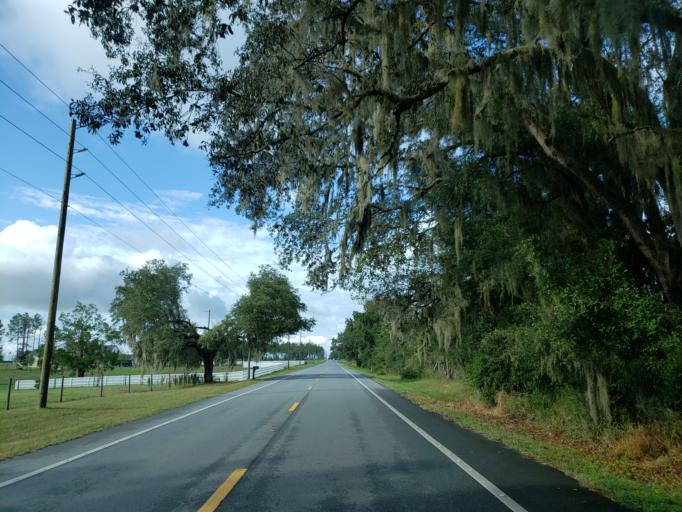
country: US
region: Florida
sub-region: Hernando County
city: Hill 'n Dale
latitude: 28.4287
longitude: -82.3028
